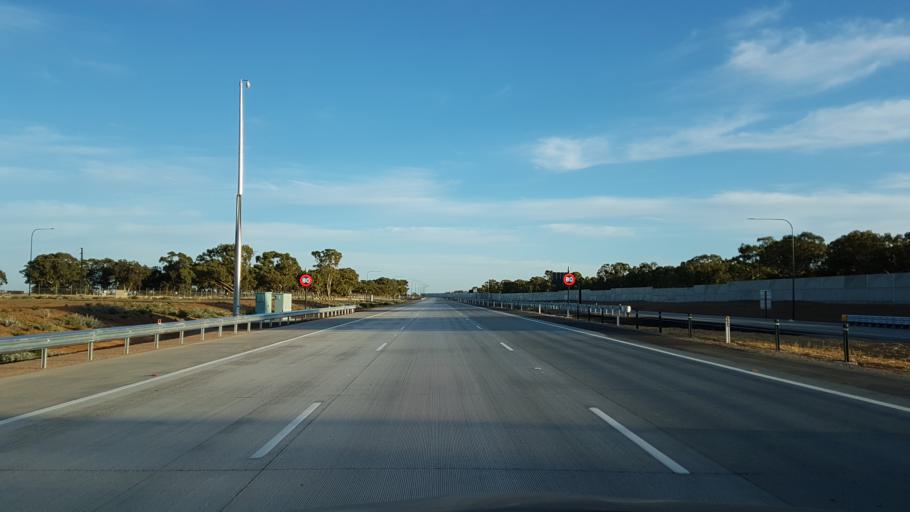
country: AU
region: South Australia
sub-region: Salisbury
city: Salisbury
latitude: -34.7641
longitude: 138.5895
